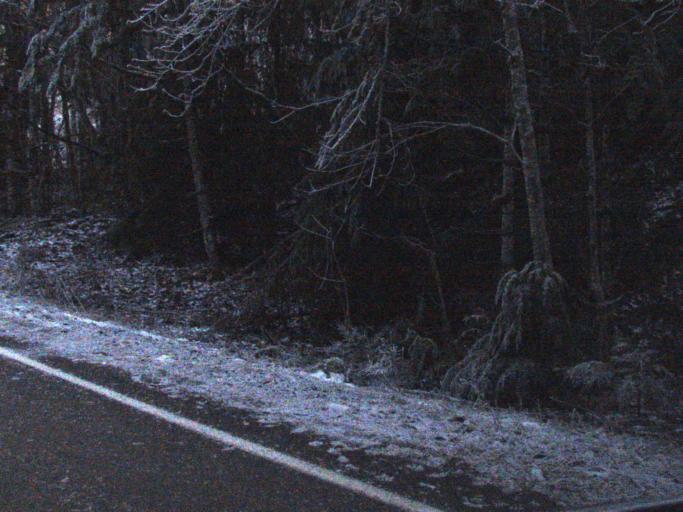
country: US
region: Washington
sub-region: Snohomish County
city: Darrington
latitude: 48.6898
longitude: -121.0987
